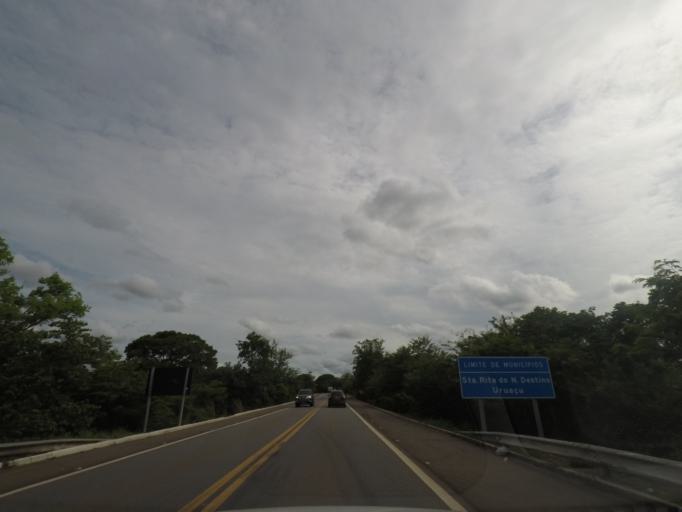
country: BR
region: Goias
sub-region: Uruacu
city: Uruacu
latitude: -14.7447
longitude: -49.0694
